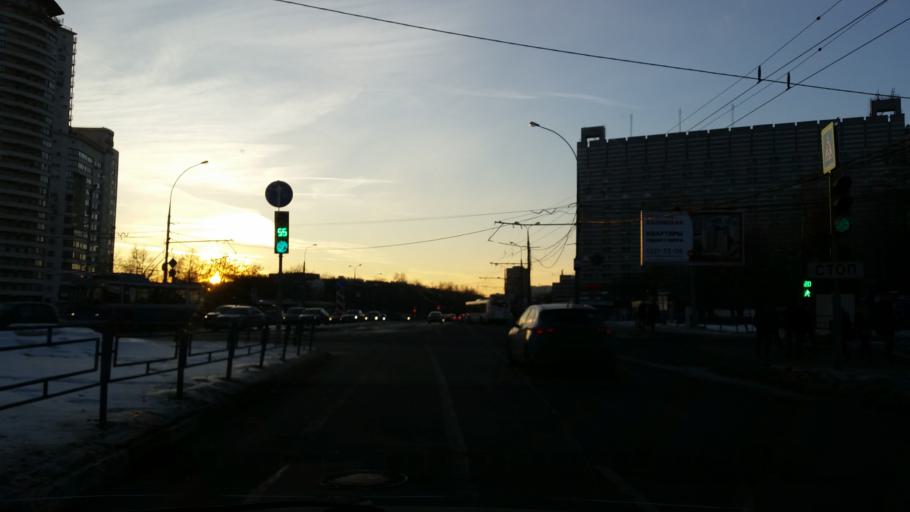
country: RU
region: Moscow
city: Kotlovka
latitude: 55.6533
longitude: 37.5988
